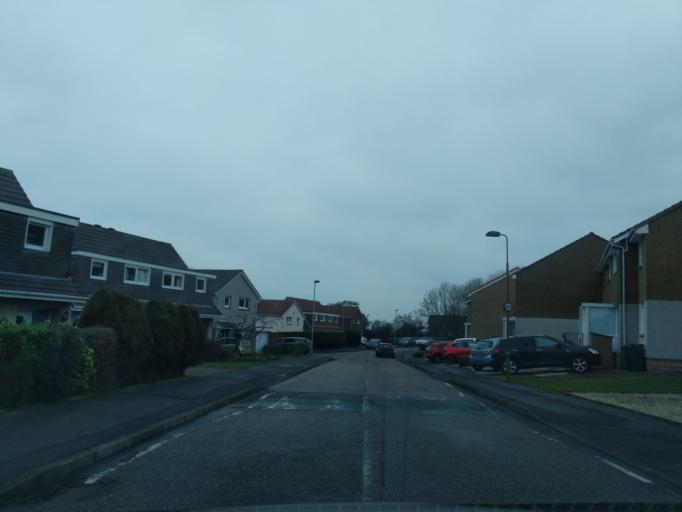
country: GB
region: Scotland
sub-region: Edinburgh
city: Balerno
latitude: 55.8945
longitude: -3.3304
